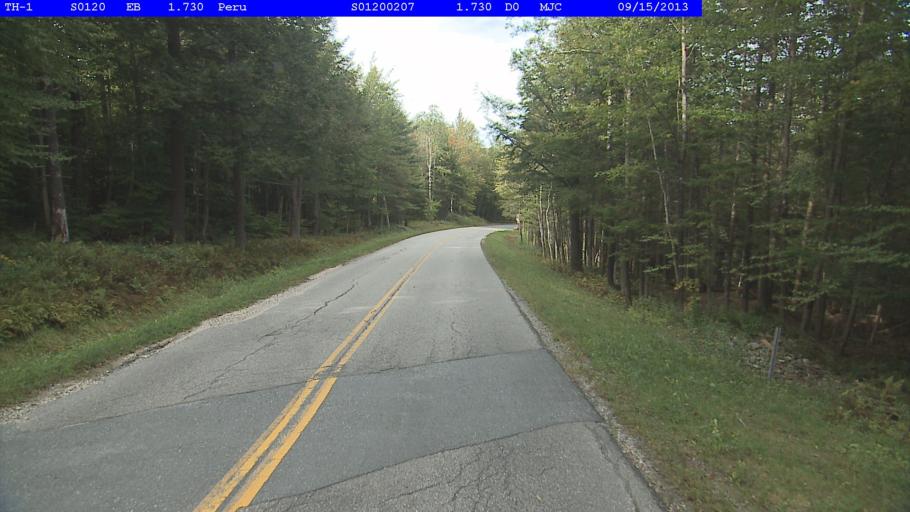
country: US
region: Vermont
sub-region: Bennington County
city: Manchester Center
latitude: 43.2493
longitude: -72.8909
